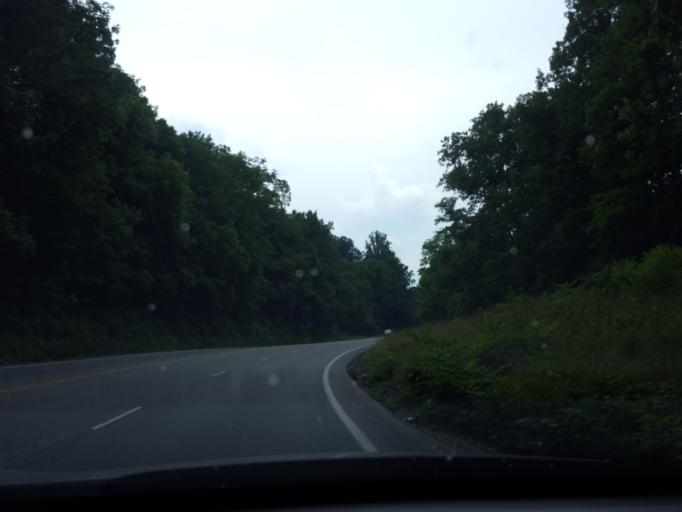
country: US
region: Virginia
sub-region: City of Waynesboro
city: Waynesboro
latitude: 38.0455
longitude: -78.8545
